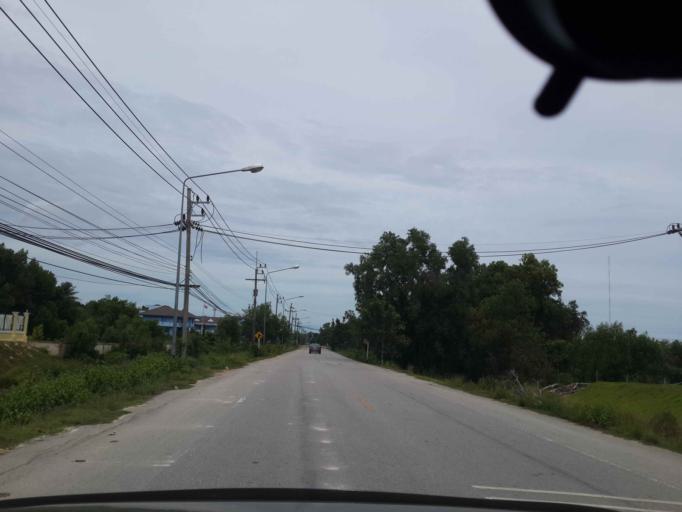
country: TH
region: Narathiwat
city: Narathiwat
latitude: 6.4321
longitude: 101.7972
